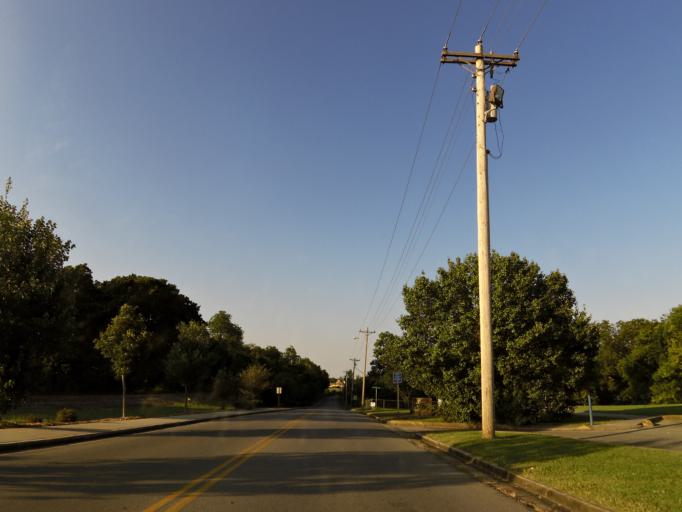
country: US
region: Tennessee
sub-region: McMinn County
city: Athens
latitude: 35.4443
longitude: -84.6011
